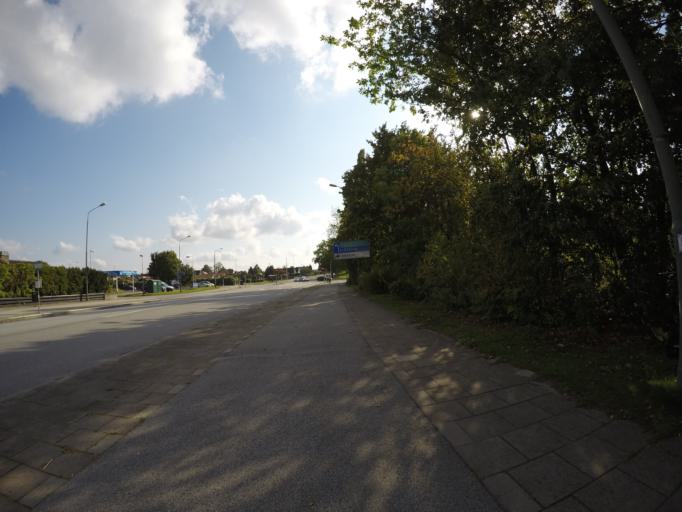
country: SE
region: Skane
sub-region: Burlovs Kommun
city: Arloev
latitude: 55.5954
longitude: 13.0740
